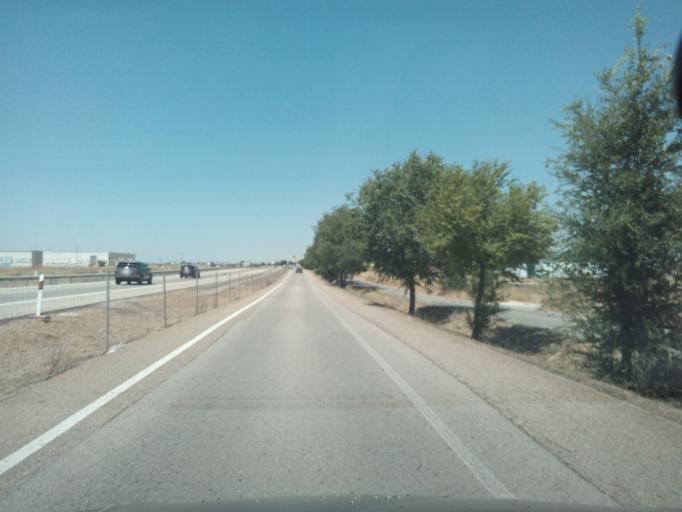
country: ES
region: Castille-La Mancha
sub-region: Province of Toledo
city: Tembleque
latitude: 39.7689
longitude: -3.4799
